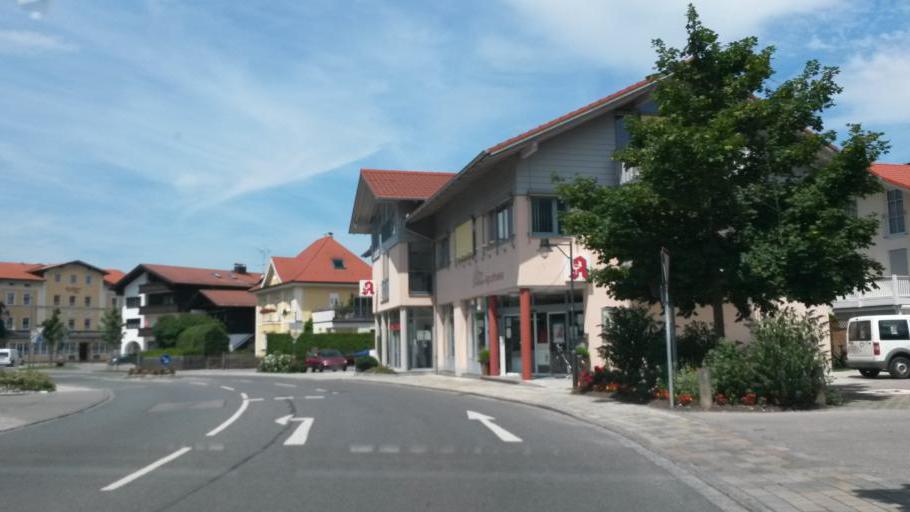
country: DE
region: Bavaria
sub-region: Upper Bavaria
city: Aschau im Chiemgau
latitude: 47.7799
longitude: 12.3249
